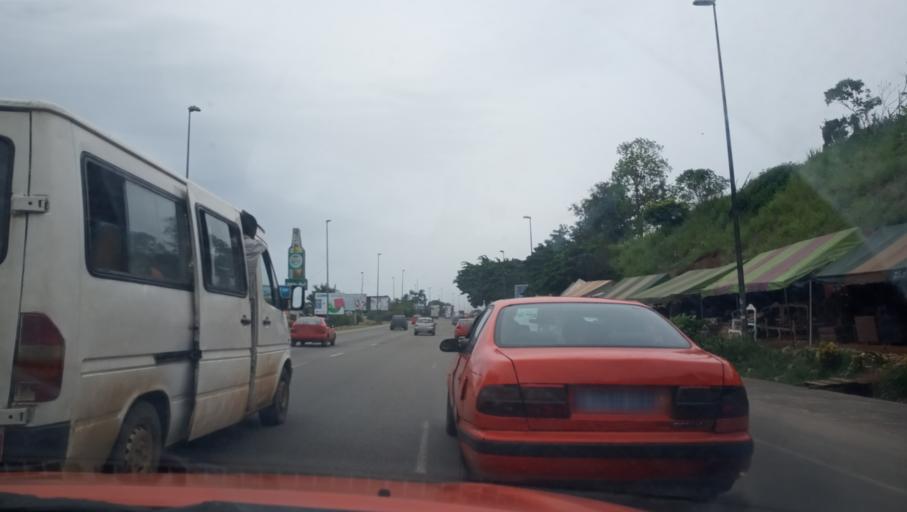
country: CI
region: Lagunes
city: Abidjan
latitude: 5.3547
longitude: -4.0090
